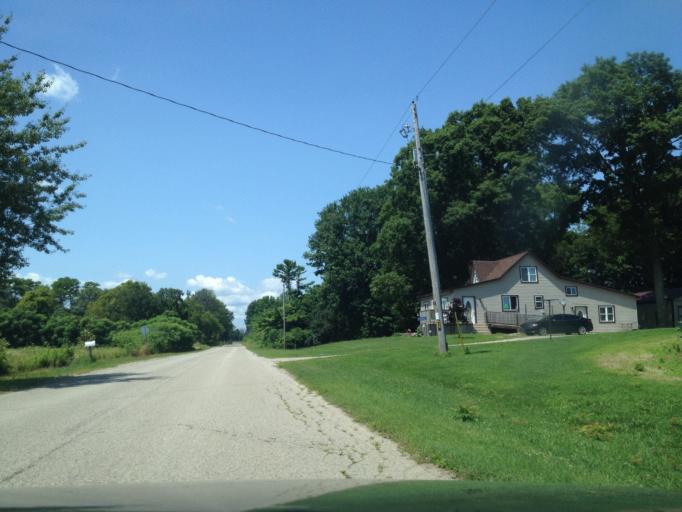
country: CA
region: Ontario
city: Aylmer
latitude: 42.6402
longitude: -80.7717
